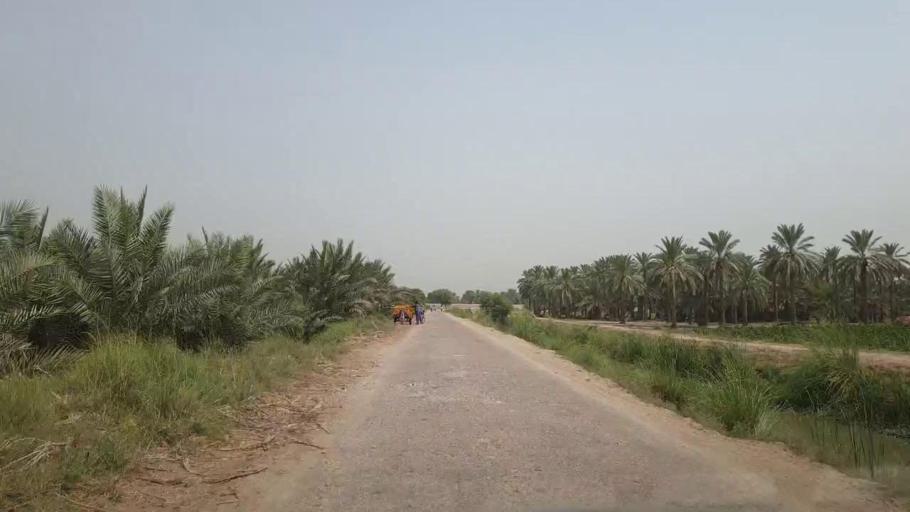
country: PK
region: Sindh
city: Gambat
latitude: 27.4344
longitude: 68.5601
